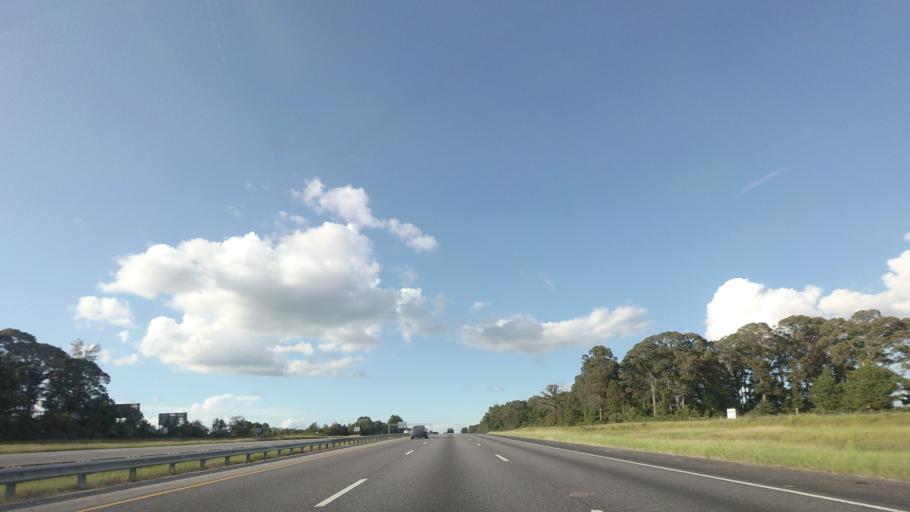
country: US
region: Georgia
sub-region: Houston County
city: Perry
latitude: 32.5496
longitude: -83.7439
